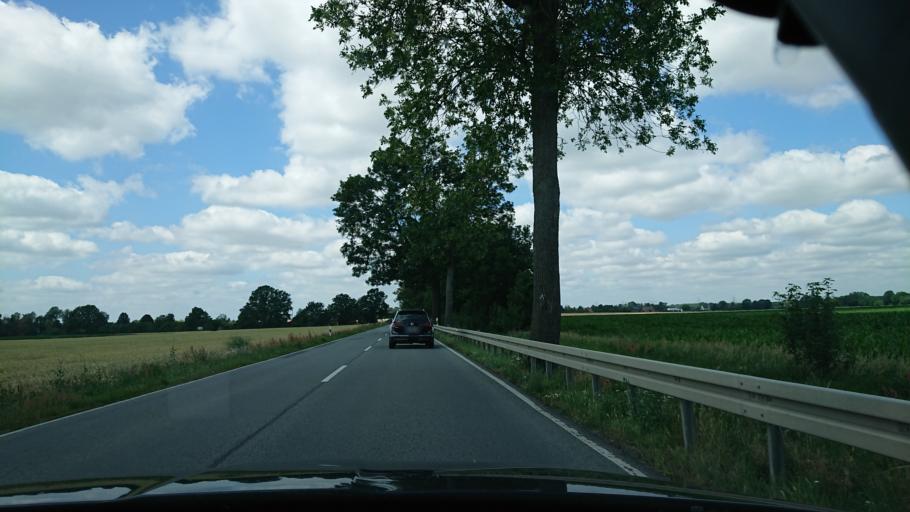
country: DE
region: Brandenburg
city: Perleberg
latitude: 53.0567
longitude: 11.9100
